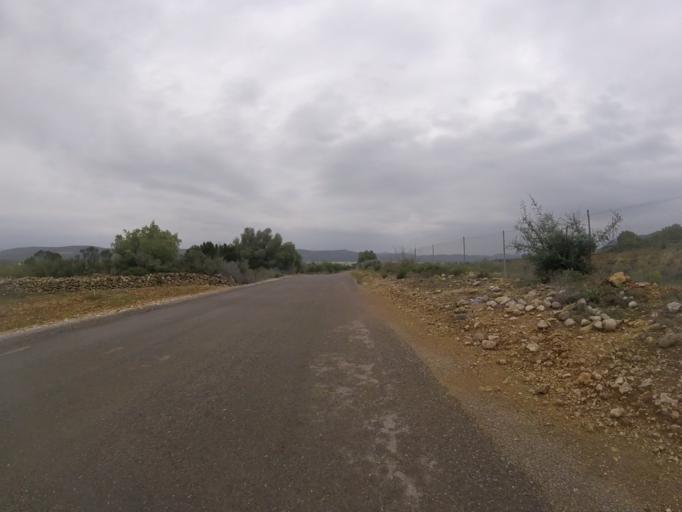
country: ES
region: Valencia
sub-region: Provincia de Castello
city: Alcala de Xivert
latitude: 40.2824
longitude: 0.2285
